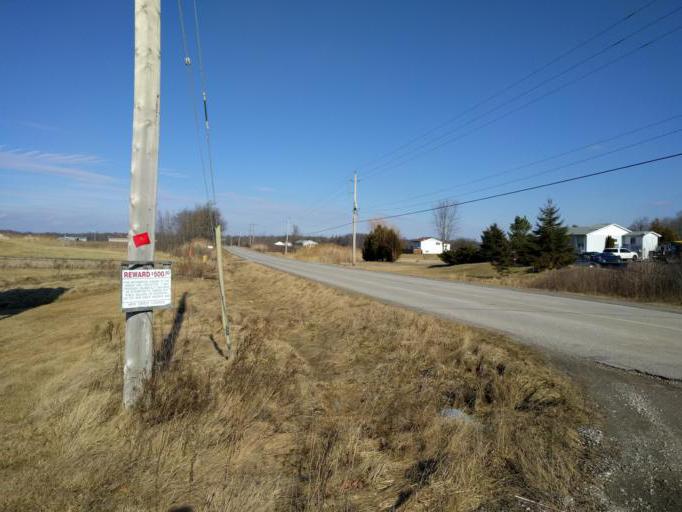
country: CA
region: Ontario
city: Brantford
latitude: 43.0093
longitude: -80.0899
